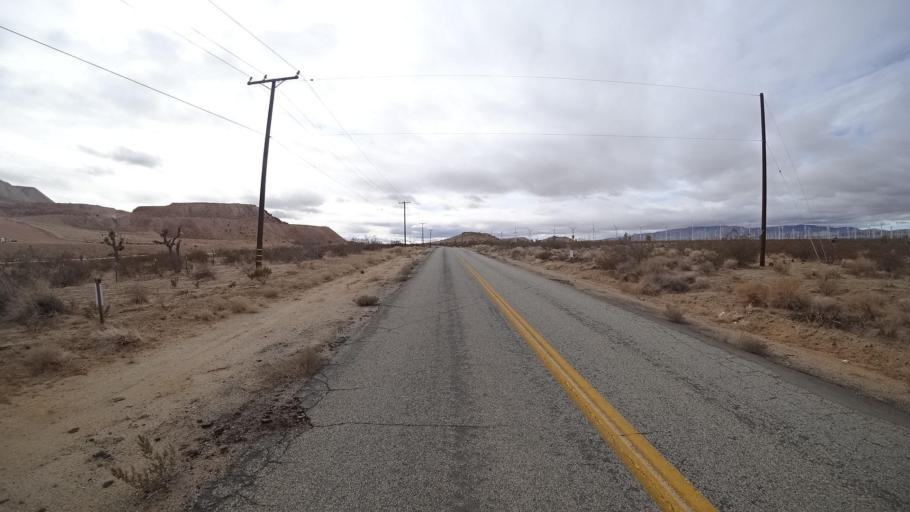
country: US
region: California
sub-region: Kern County
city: Mojave
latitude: 34.9945
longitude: -118.2013
